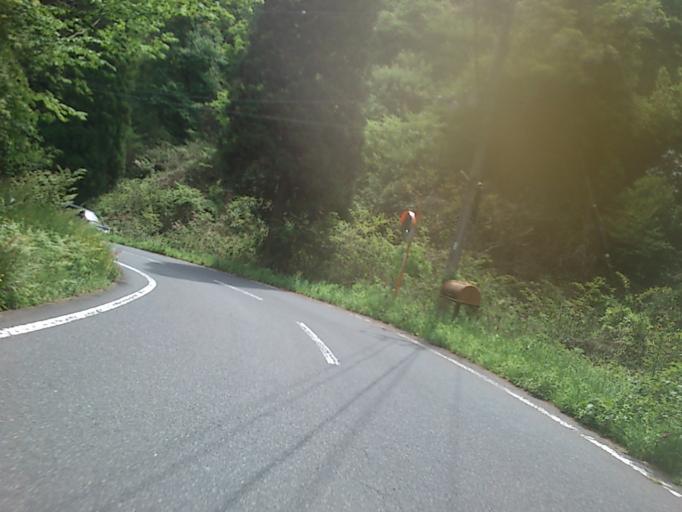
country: JP
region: Kyoto
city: Miyazu
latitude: 35.5866
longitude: 135.1226
